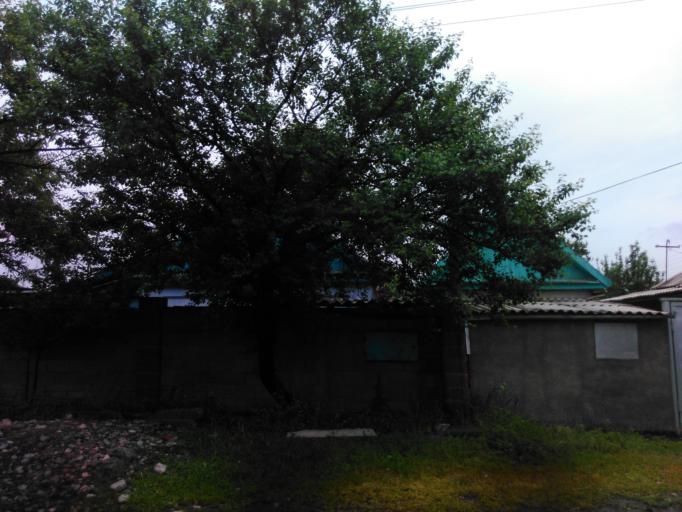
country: KG
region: Chuy
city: Tokmok
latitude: 42.8147
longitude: 75.3238
